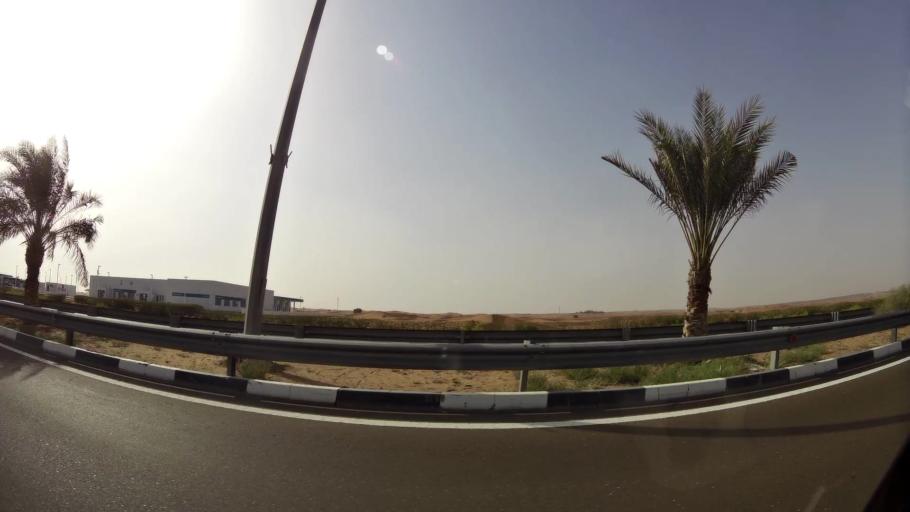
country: AE
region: Abu Dhabi
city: Al Ain
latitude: 24.2191
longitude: 55.6410
